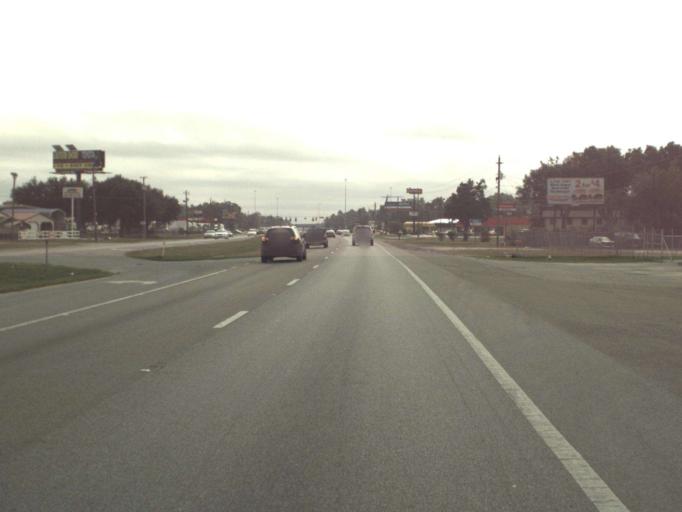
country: US
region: Florida
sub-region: Escambia County
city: Ensley
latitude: 30.5144
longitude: -87.2716
